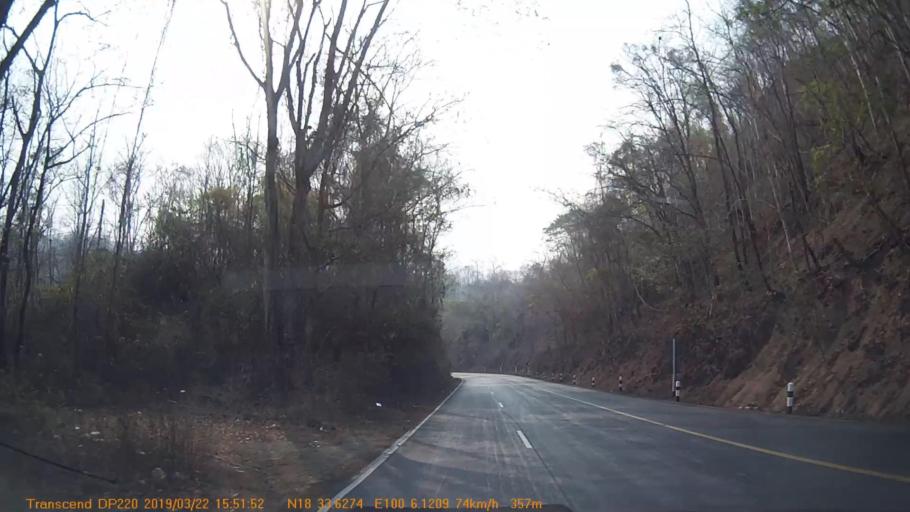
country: TH
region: Phrae
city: Song
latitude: 18.5605
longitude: 100.1017
